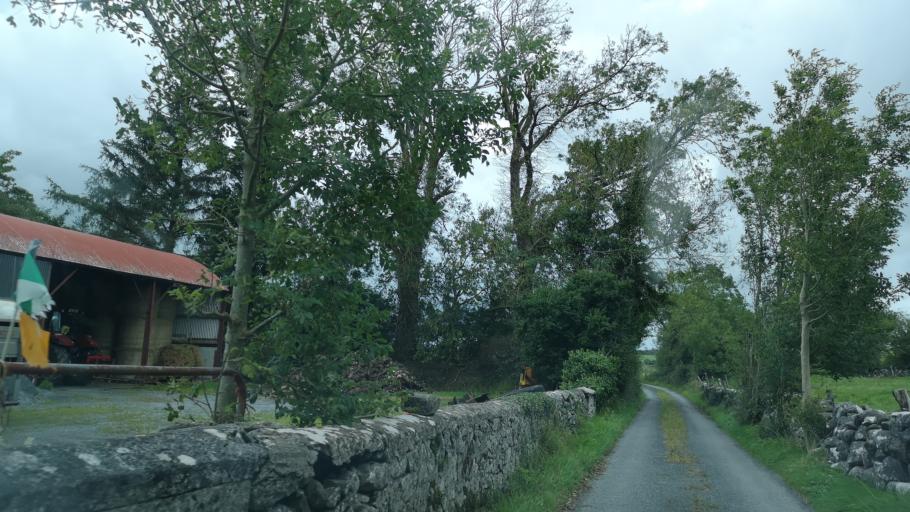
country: IE
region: Connaught
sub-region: County Galway
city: Athenry
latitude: 53.3343
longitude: -8.7817
